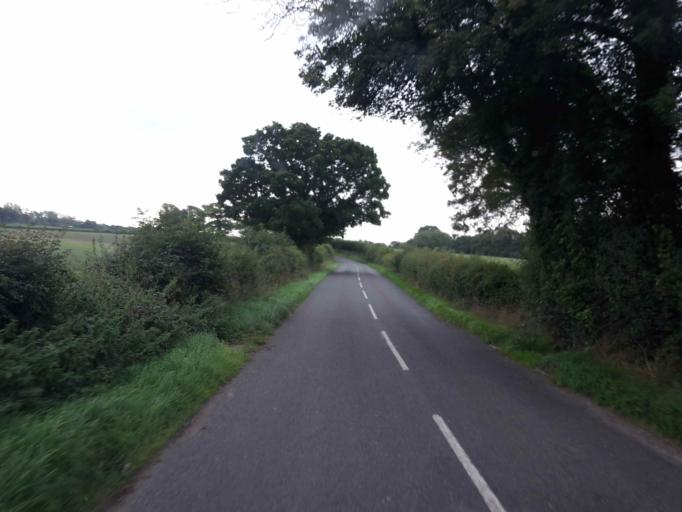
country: GB
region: England
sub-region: West Sussex
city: Rudgwick
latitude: 51.0733
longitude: -0.4516
